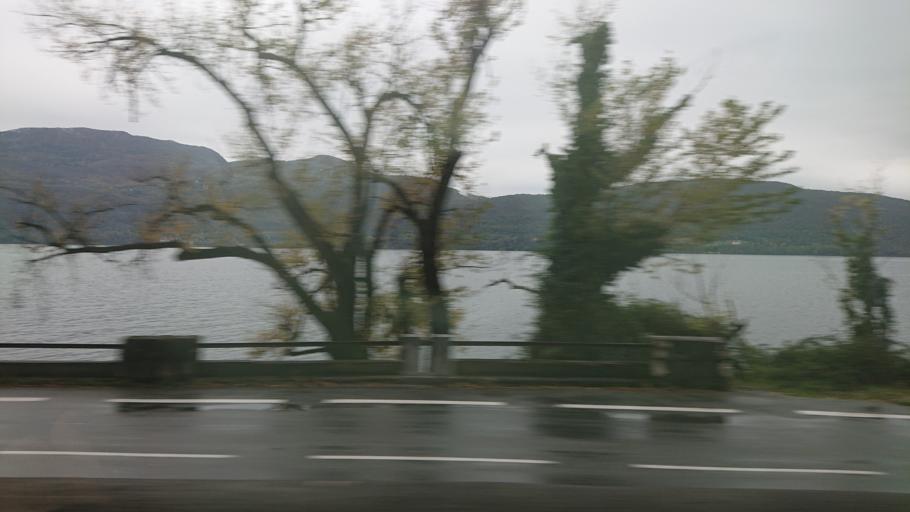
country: FR
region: Rhone-Alpes
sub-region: Departement de la Savoie
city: Chatillon
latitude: 45.7745
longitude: 5.8667
